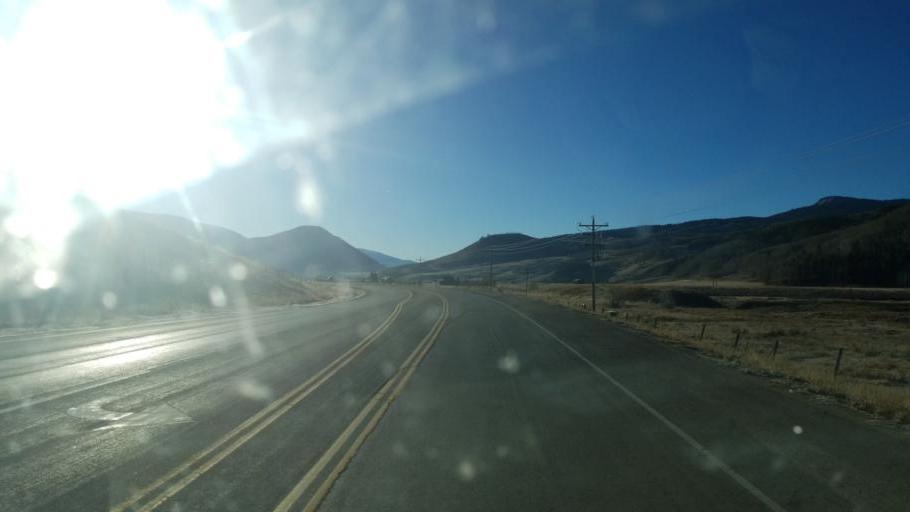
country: US
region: Colorado
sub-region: Gunnison County
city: Crested Butte
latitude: 38.8419
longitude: -106.9414
